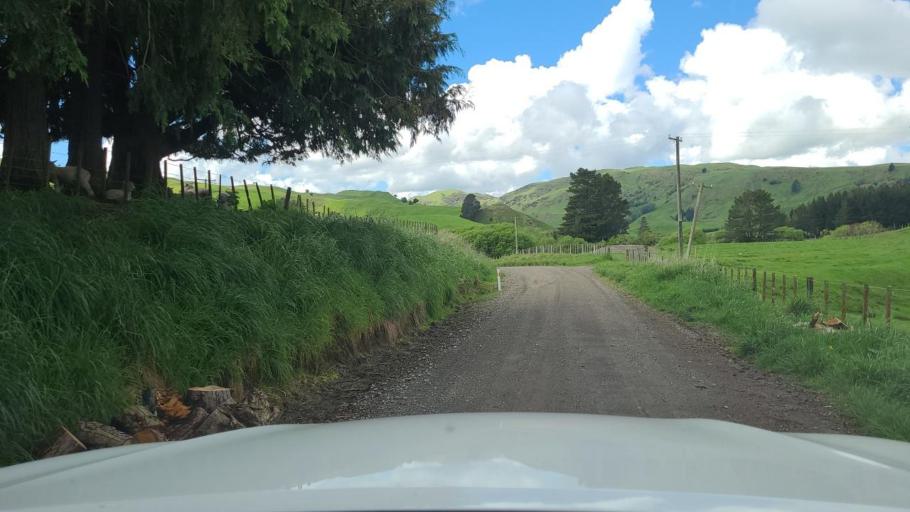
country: NZ
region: Hawke's Bay
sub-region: Napier City
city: Taradale
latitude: -39.2777
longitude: 176.5534
